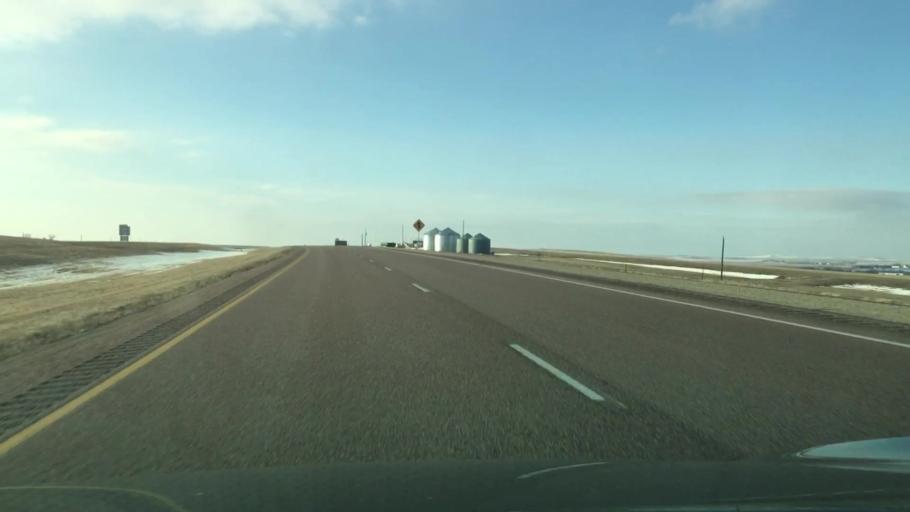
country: US
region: South Dakota
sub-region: Lyman County
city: Kennebec
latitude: 43.8966
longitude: -99.8691
